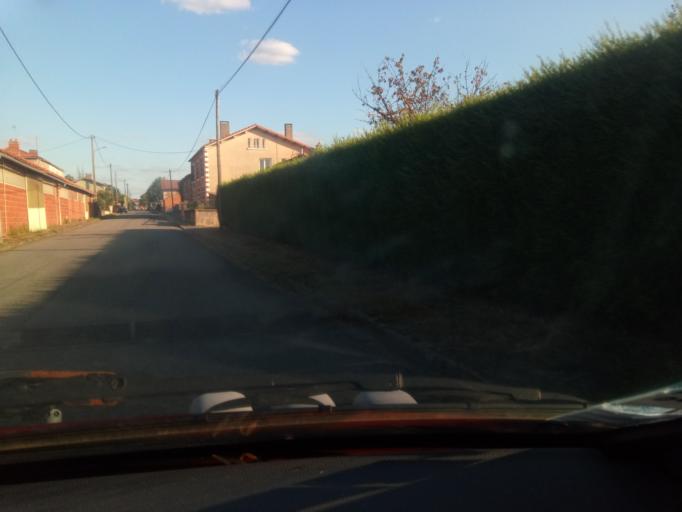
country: FR
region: Poitou-Charentes
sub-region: Departement de la Vienne
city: Availles-Limouzine
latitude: 46.1241
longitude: 0.7275
